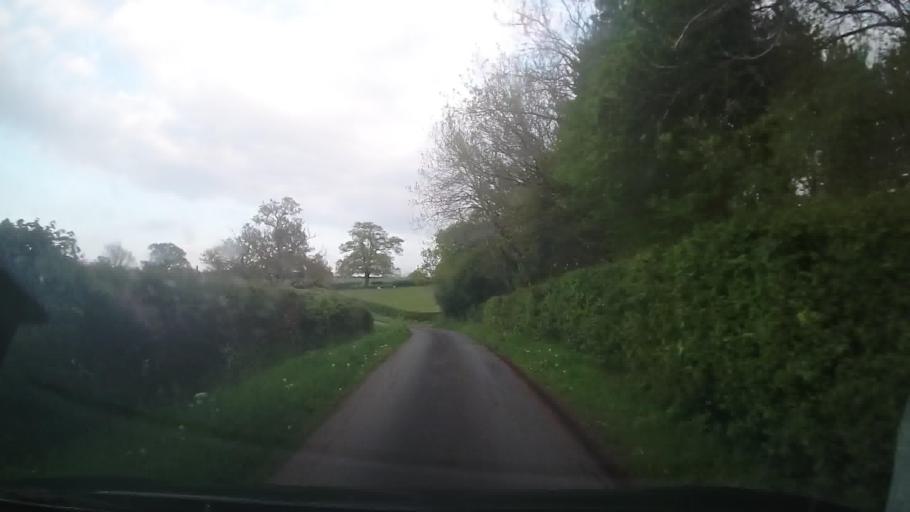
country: GB
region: England
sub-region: Shropshire
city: Ellesmere
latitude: 52.9385
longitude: -2.8653
